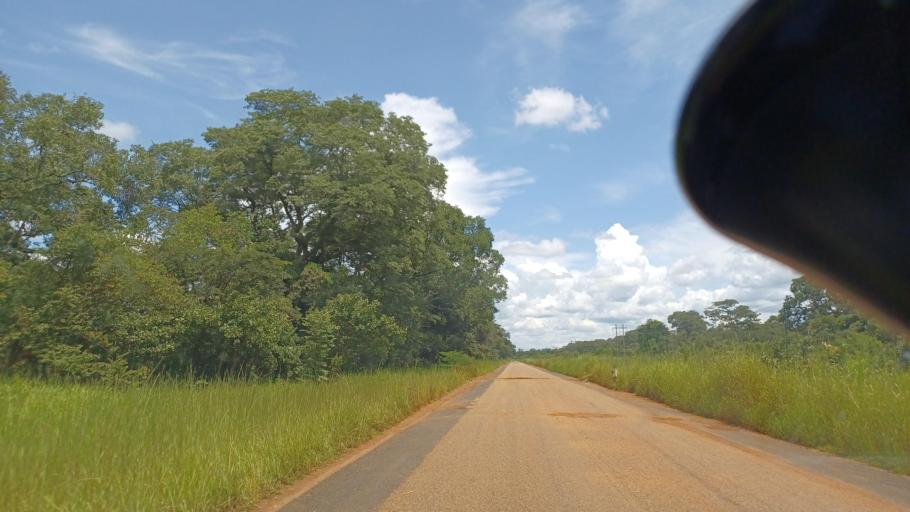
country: ZM
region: North-Western
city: Solwezi
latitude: -12.5737
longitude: 26.1342
